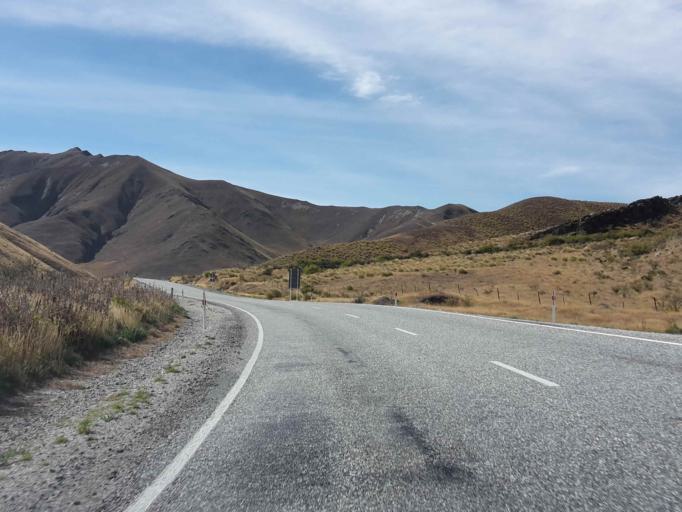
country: NZ
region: Otago
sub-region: Queenstown-Lakes District
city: Wanaka
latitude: -44.5796
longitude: 169.6124
